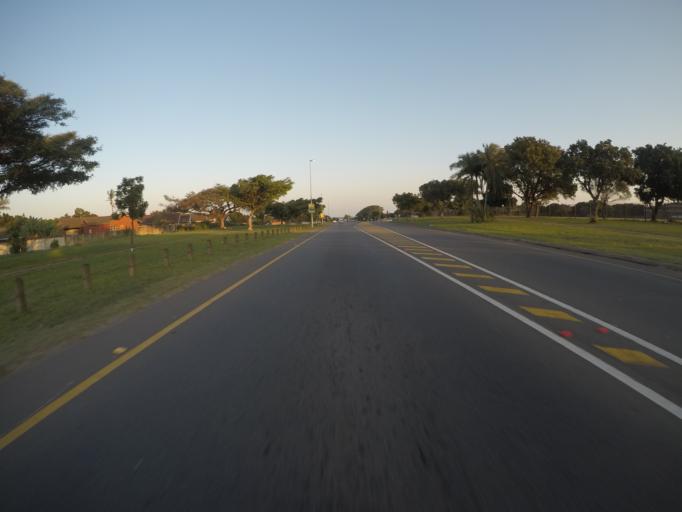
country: ZA
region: KwaZulu-Natal
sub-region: uThungulu District Municipality
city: Richards Bay
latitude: -28.7597
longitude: 32.0588
